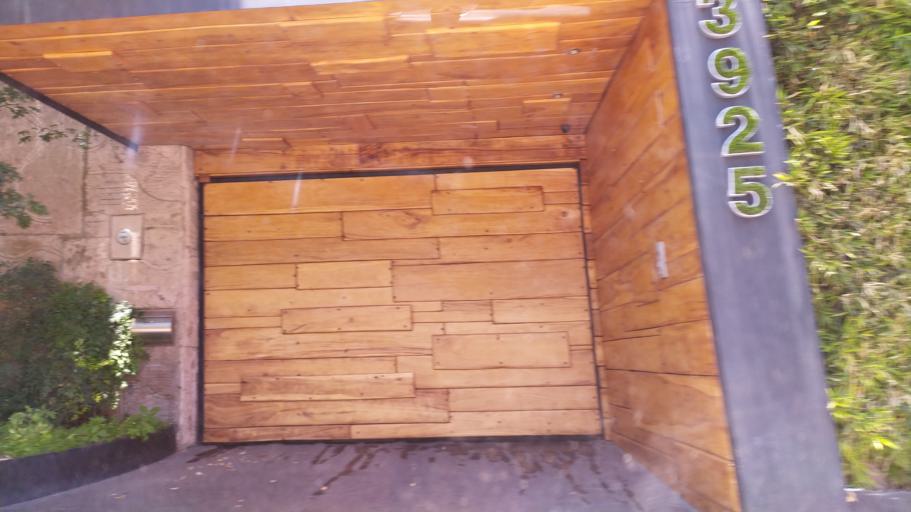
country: MX
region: Jalisco
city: Guadalajara
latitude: 20.6862
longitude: -103.4072
